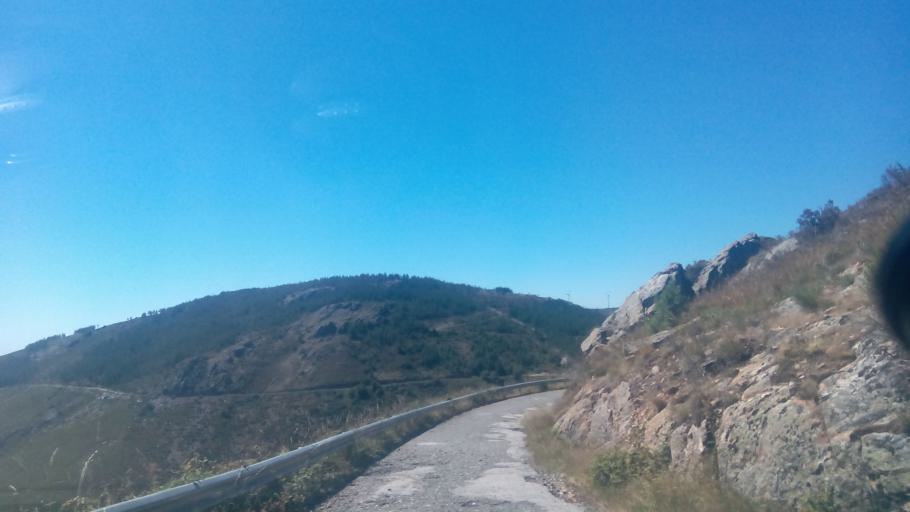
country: PT
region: Vila Real
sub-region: Mesao Frio
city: Mesao Frio
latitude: 41.2677
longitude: -7.9073
